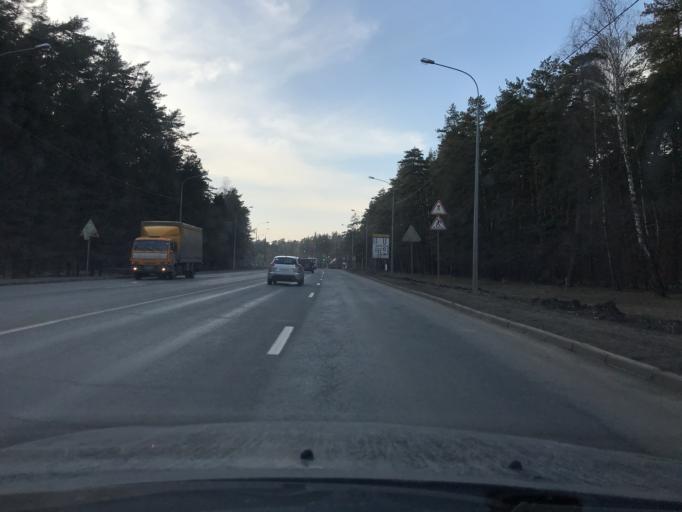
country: RU
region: Kaluga
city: Kaluga
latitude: 54.5195
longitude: 36.1990
